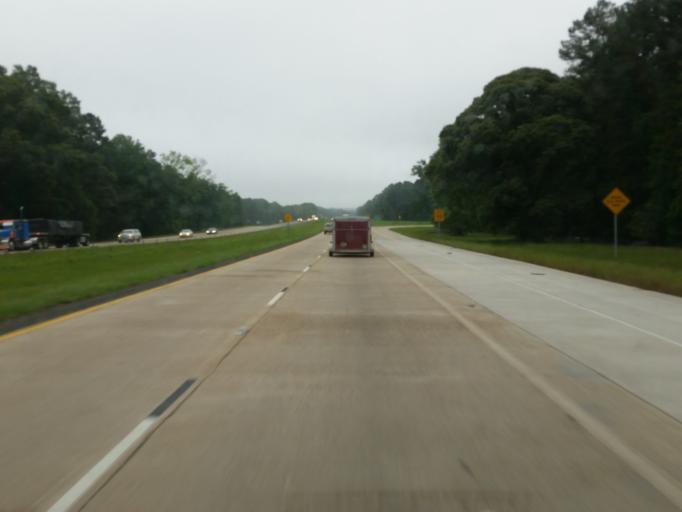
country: US
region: Louisiana
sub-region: Webster Parish
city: Minden
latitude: 32.5888
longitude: -93.3417
